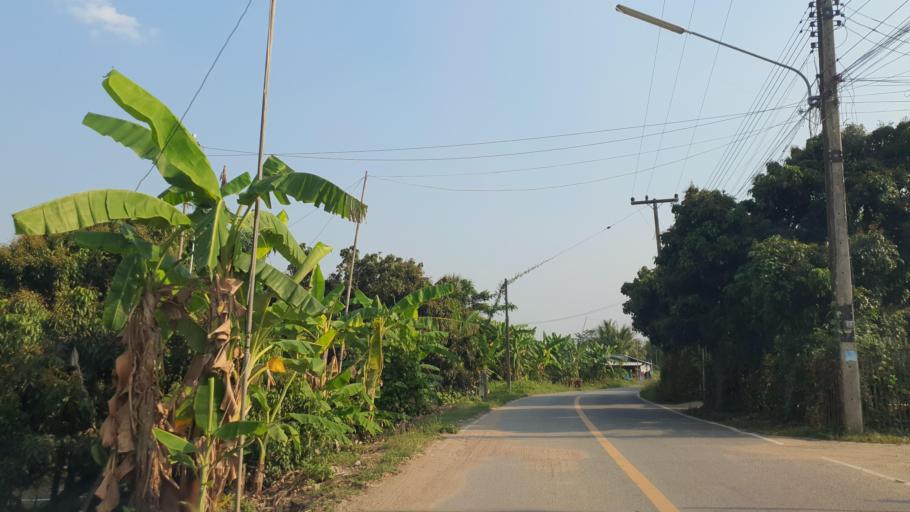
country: TH
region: Chiang Mai
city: Mae Wang
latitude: 18.6583
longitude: 98.8186
